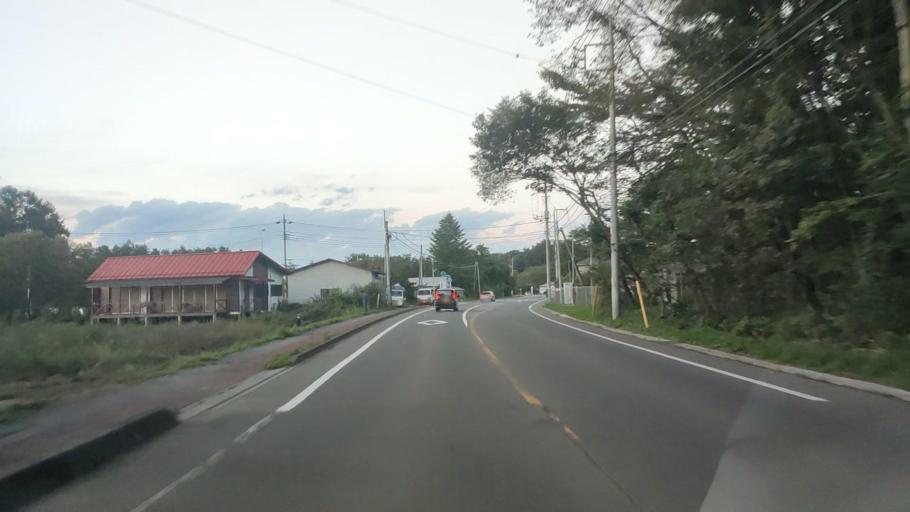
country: JP
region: Nagano
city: Komoro
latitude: 36.5063
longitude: 138.5924
